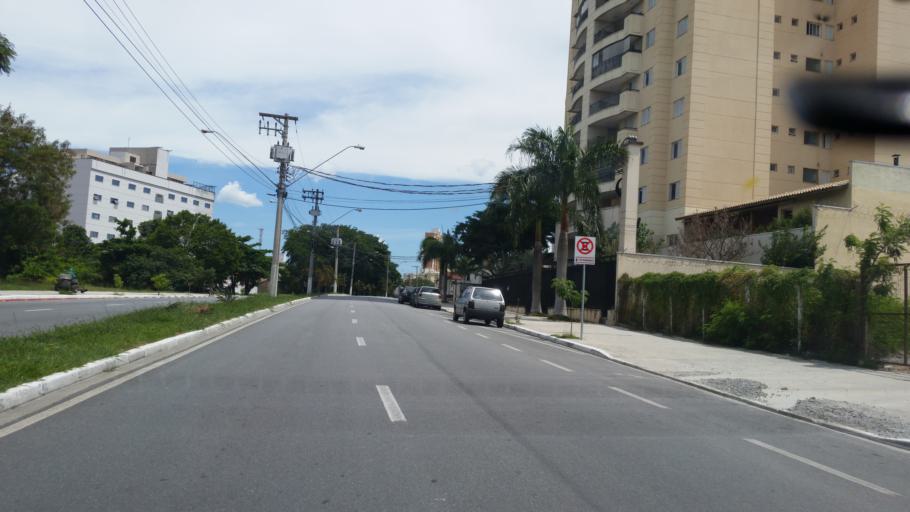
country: BR
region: Sao Paulo
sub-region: Taubate
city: Taubate
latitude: -23.0220
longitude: -45.5808
